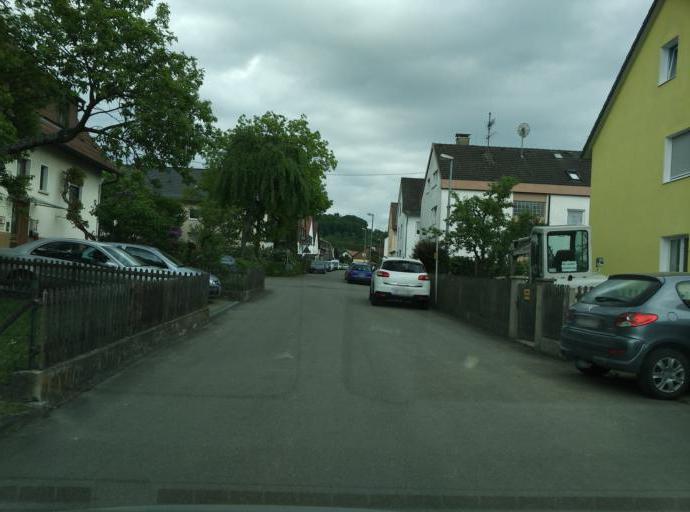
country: DE
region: Baden-Wuerttemberg
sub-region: Regierungsbezirk Stuttgart
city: Frickenhausen
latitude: 48.5946
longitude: 9.3641
